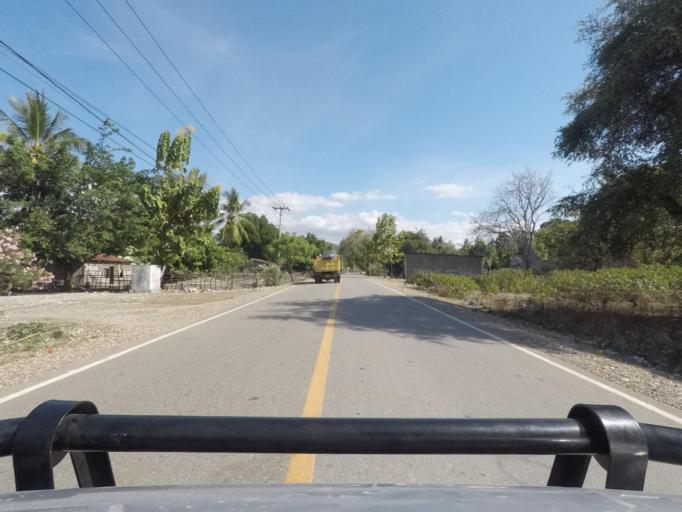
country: ID
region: East Nusa Tenggara
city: Atambua
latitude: -8.9422
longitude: 124.9781
